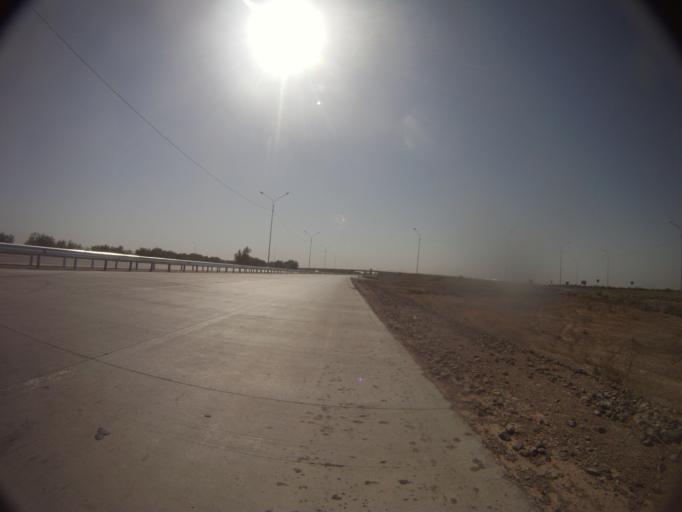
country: KZ
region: Ongtustik Qazaqstan
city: Turkestan
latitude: 43.2132
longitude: 68.4749
